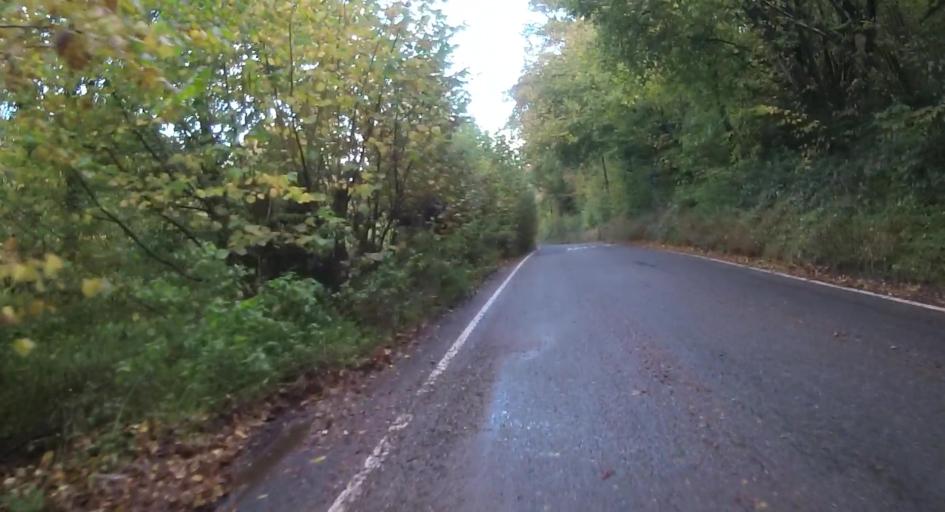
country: GB
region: England
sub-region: Hampshire
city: Four Marks
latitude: 51.1393
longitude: -1.0262
